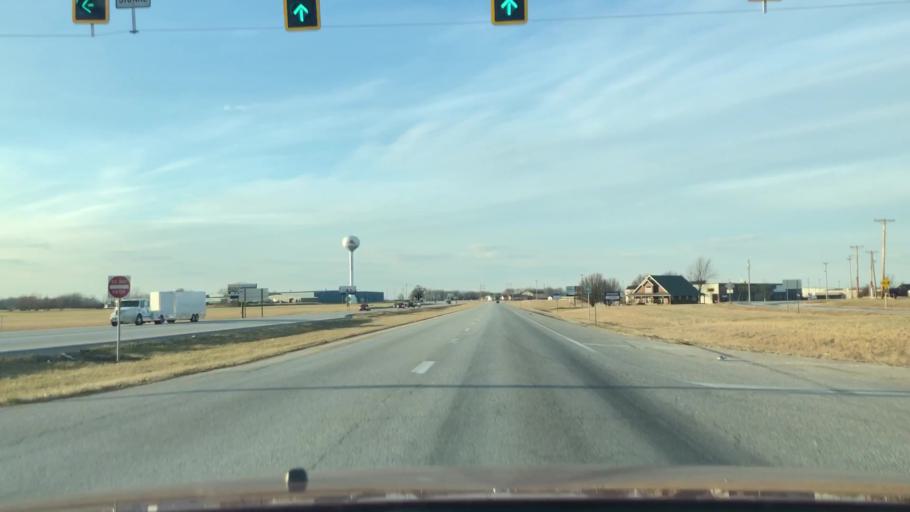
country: US
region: Missouri
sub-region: Webster County
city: Seymour
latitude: 37.1501
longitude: -92.7534
